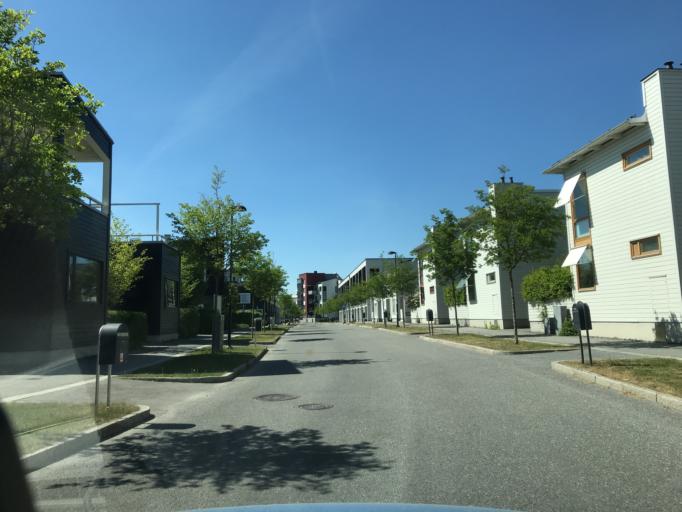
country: SE
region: Stockholm
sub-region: Solna Kommun
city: Rasunda
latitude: 59.4028
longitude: 17.9849
